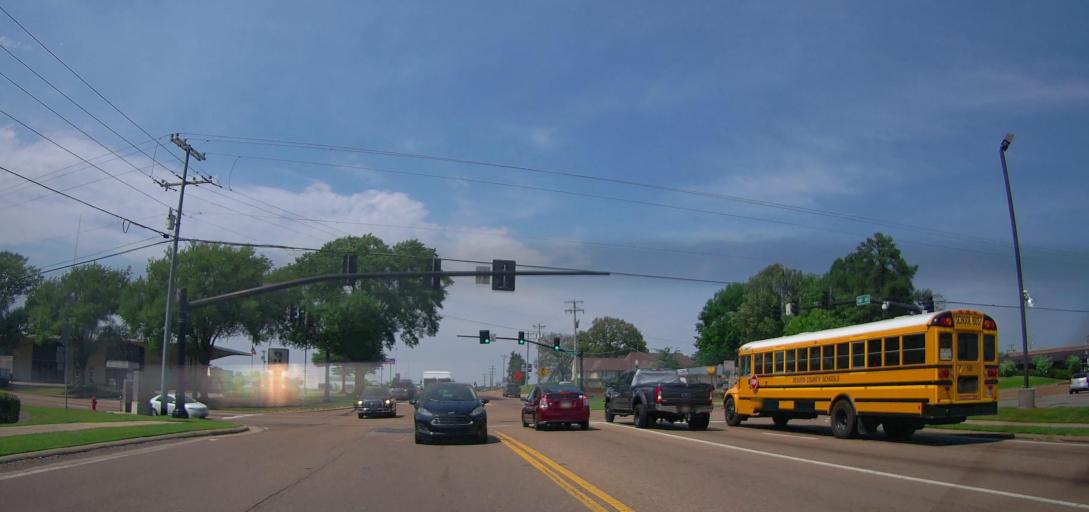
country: US
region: Mississippi
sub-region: De Soto County
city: Olive Branch
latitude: 34.9615
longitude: -89.8304
